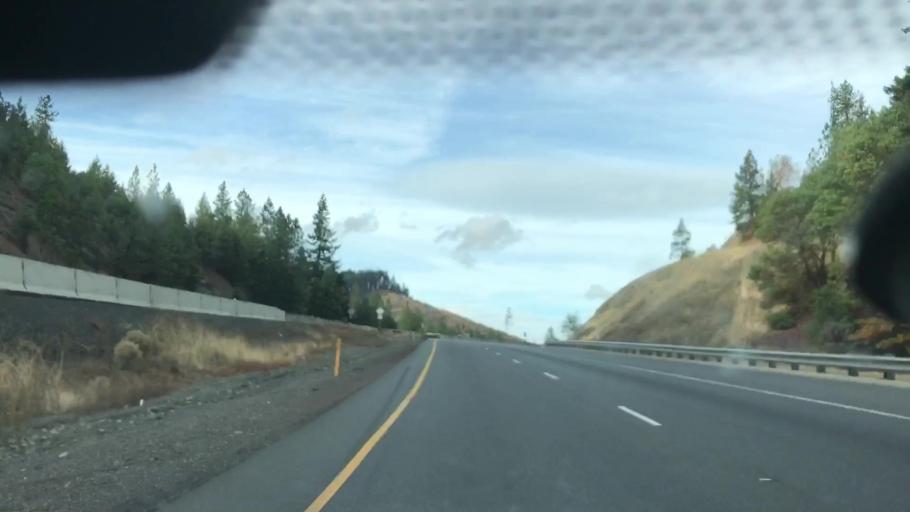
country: US
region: Oregon
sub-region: Josephine County
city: Merlin
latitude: 42.6575
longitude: -123.3761
